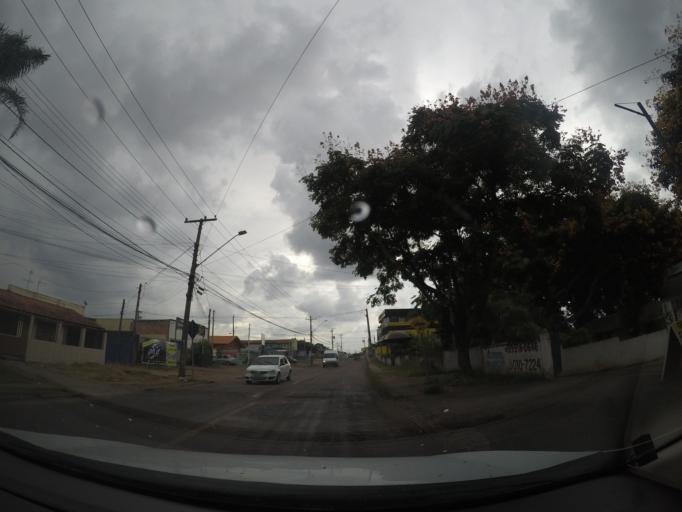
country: BR
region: Parana
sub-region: Sao Jose Dos Pinhais
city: Sao Jose dos Pinhais
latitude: -25.5343
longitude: -49.2431
